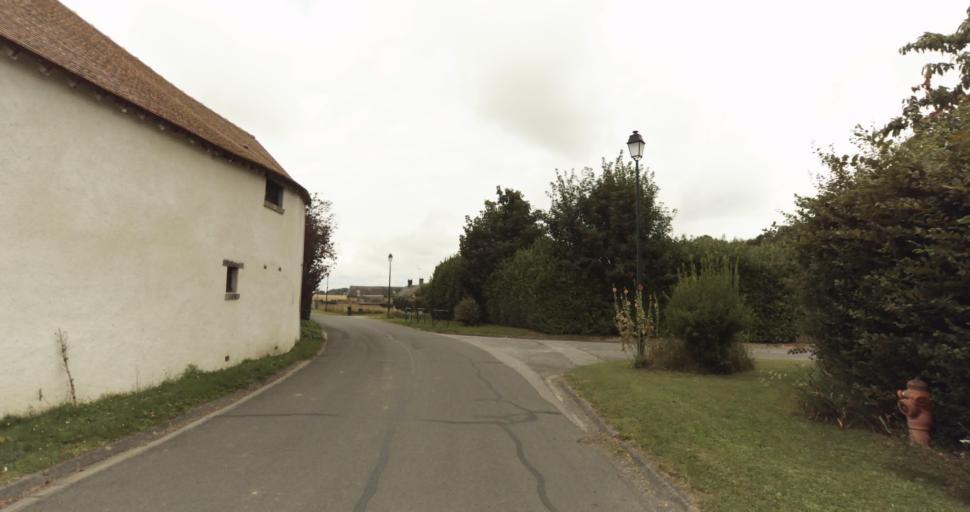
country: FR
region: Haute-Normandie
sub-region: Departement de l'Eure
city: La Couture-Boussey
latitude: 48.9461
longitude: 1.3648
